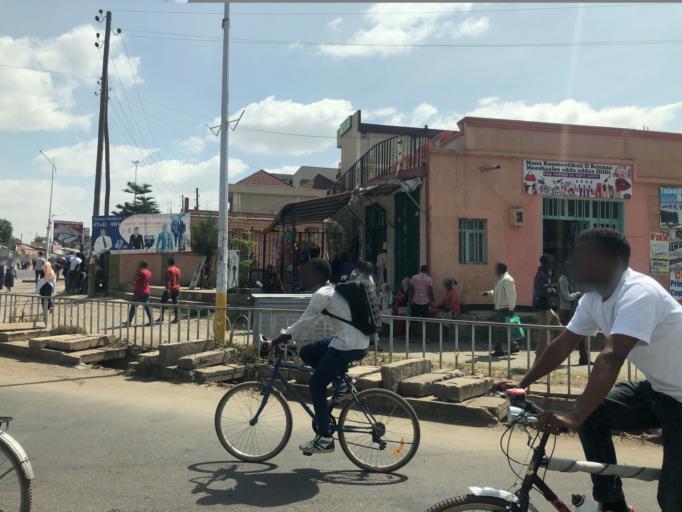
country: ET
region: Oromiya
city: Shashemene
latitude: 7.2036
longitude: 38.6089
